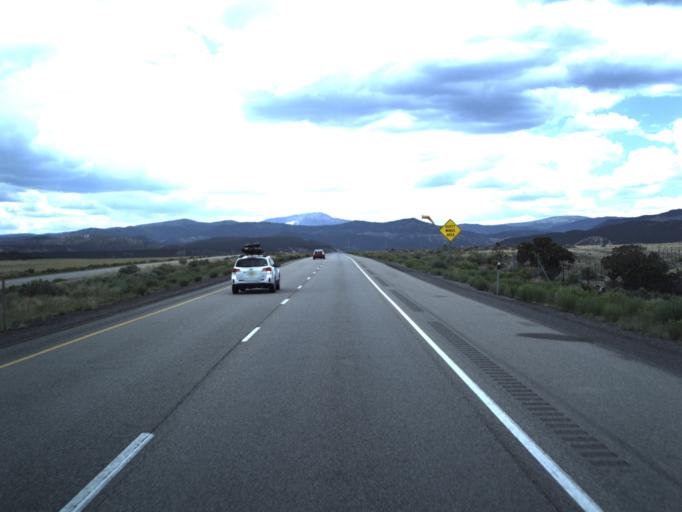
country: US
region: Utah
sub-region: Emery County
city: Ferron
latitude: 38.7812
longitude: -111.3096
